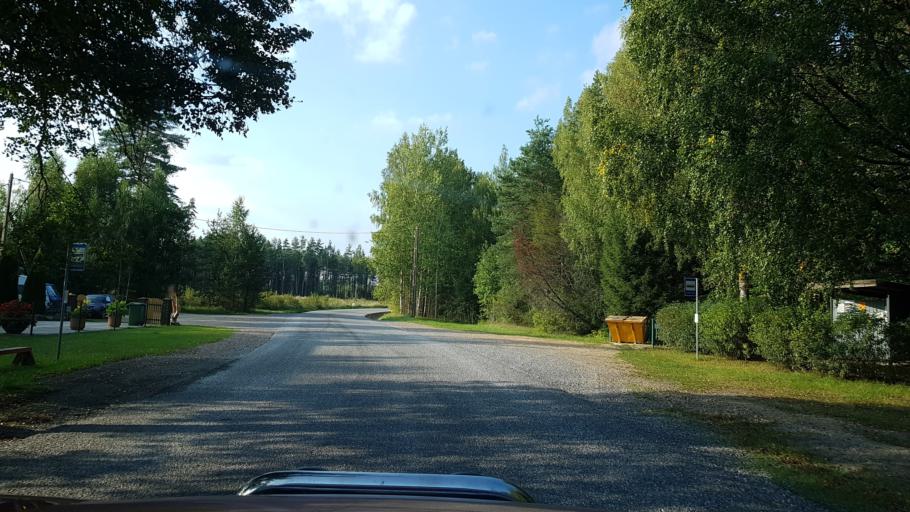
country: EE
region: Polvamaa
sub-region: Polva linn
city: Polva
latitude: 58.1282
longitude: 26.9232
